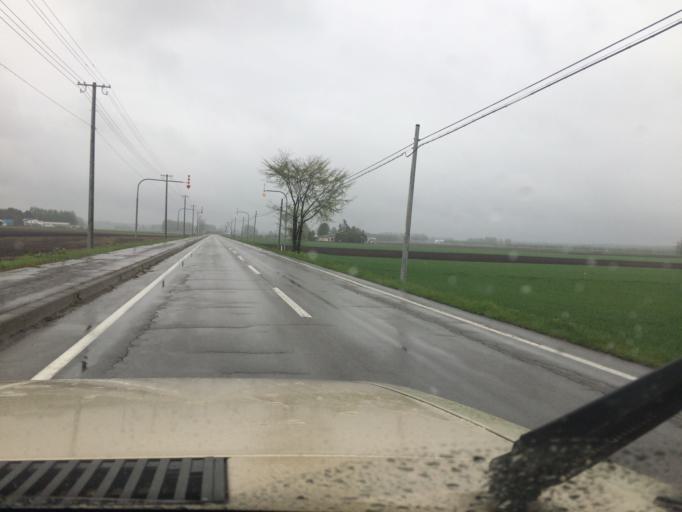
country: JP
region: Hokkaido
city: Obihiro
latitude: 42.8389
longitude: 142.9960
